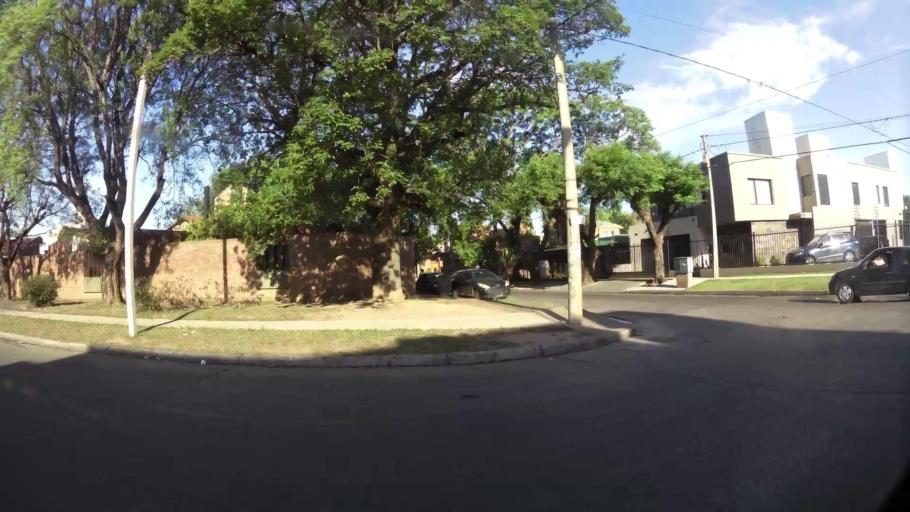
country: AR
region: Cordoba
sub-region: Departamento de Capital
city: Cordoba
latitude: -31.3703
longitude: -64.2265
